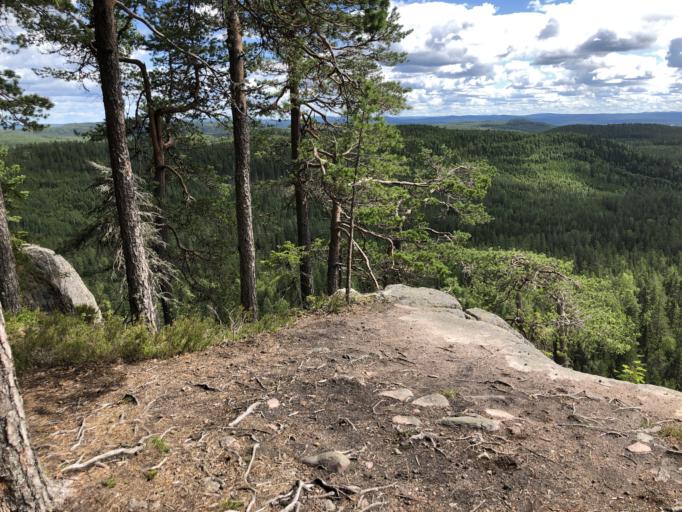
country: SE
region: Dalarna
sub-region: Vansbro Kommun
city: Vansbro
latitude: 60.6641
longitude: 14.2705
